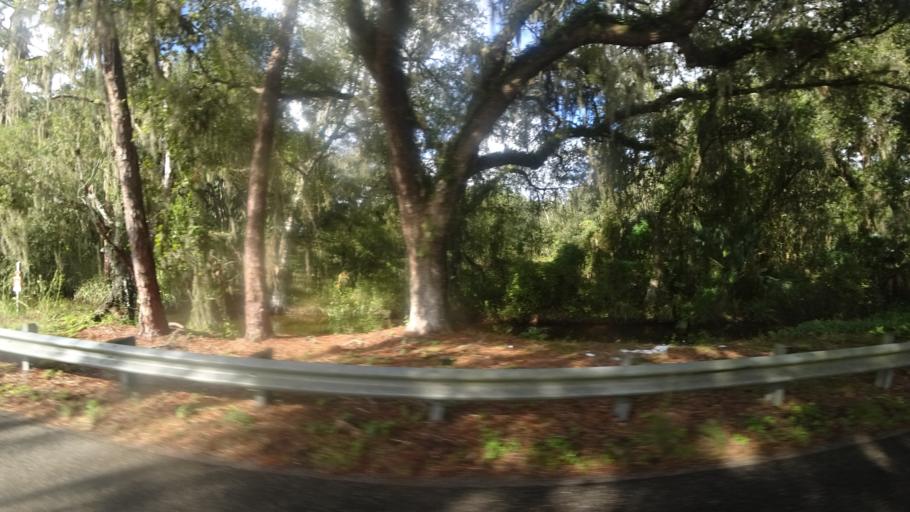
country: US
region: Florida
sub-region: Manatee County
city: Ellenton
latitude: 27.5850
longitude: -82.4091
